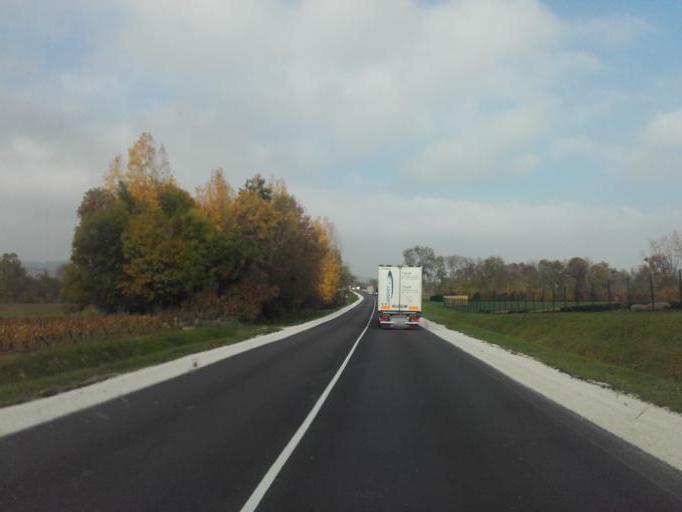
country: FR
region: Bourgogne
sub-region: Departement de la Cote-d'Or
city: Meursault
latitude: 46.9823
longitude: 4.7899
